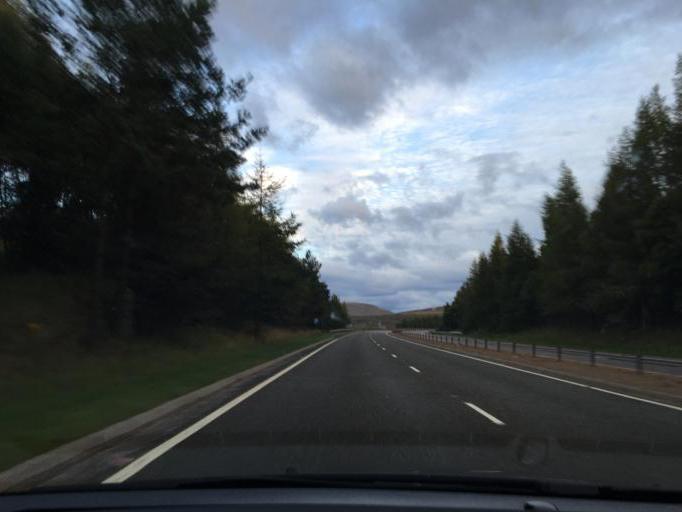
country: GB
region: Scotland
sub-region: Highland
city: Aviemore
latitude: 57.3382
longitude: -3.9848
